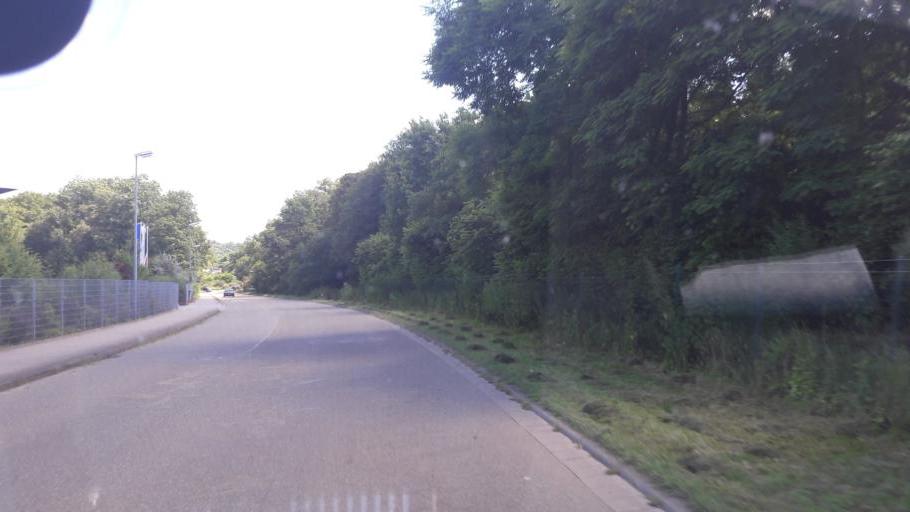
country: DE
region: Baden-Wuerttemberg
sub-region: Karlsruhe Region
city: Karlsdorf-Neuthard
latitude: 49.1198
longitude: 8.5624
